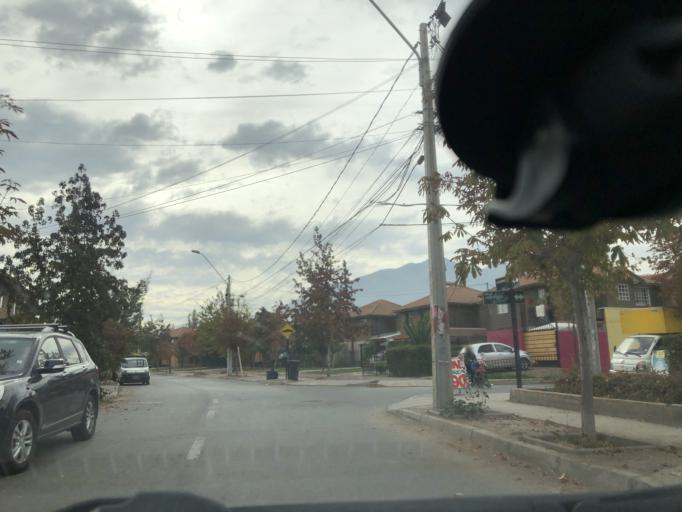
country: CL
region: Santiago Metropolitan
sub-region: Provincia de Cordillera
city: Puente Alto
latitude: -33.6133
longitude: -70.5237
